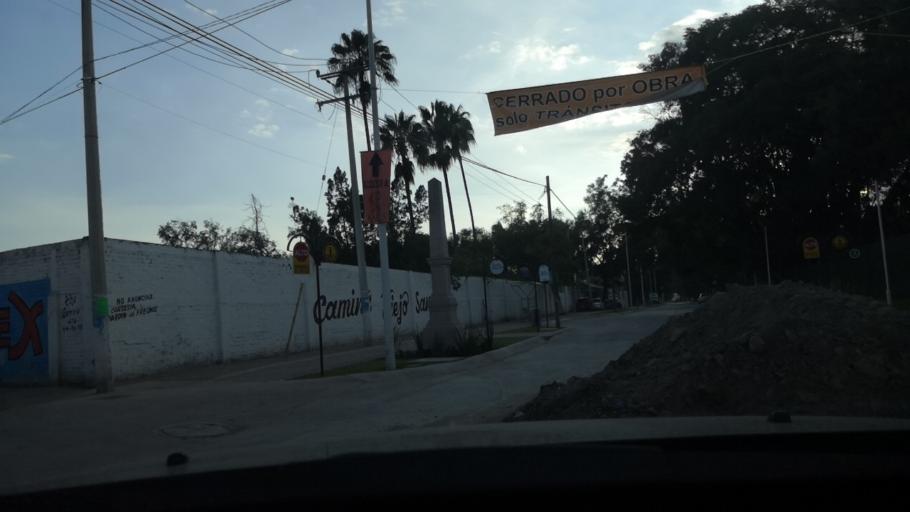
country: MX
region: Guanajuato
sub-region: San Francisco del Rincon
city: Fraccionamiento la Mezquitera
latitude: 21.0250
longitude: -101.8398
